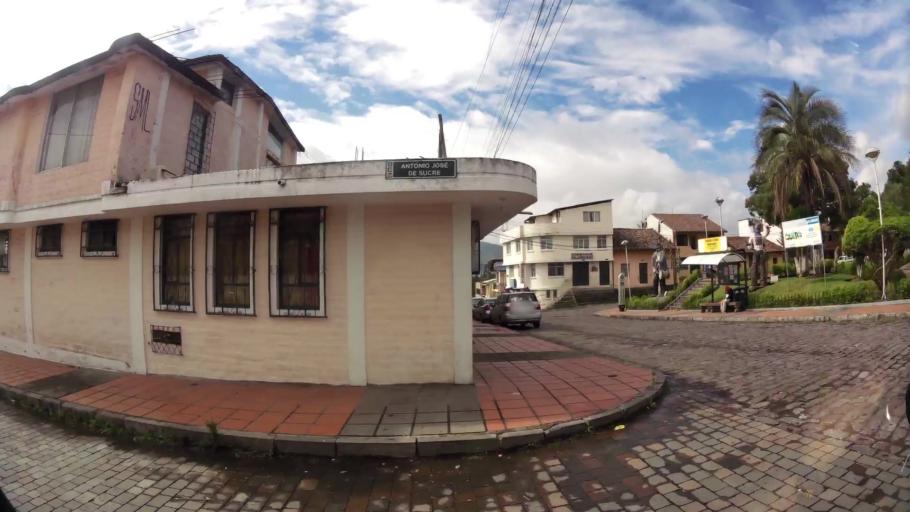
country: EC
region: Pichincha
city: Sangolqui
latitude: -0.3083
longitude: -78.4155
